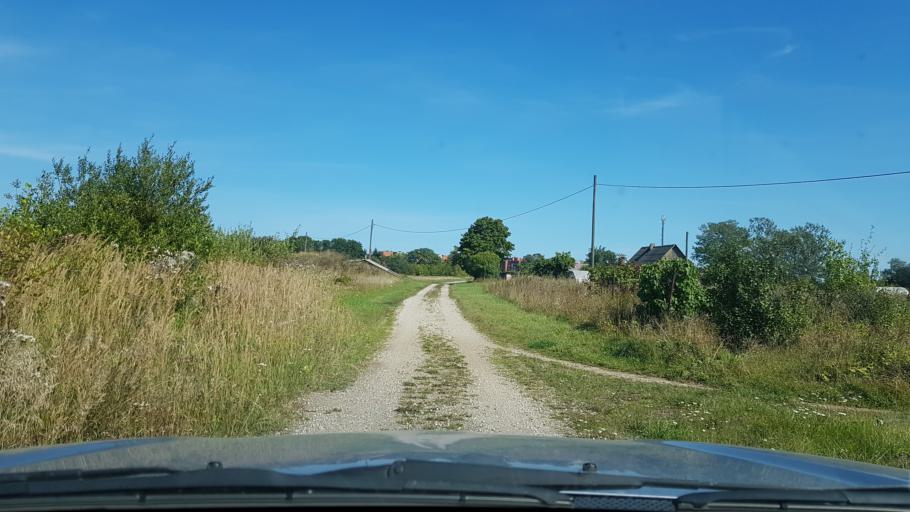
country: EE
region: Ida-Virumaa
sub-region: Sillamaee linn
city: Sillamae
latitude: 59.3875
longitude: 27.7786
